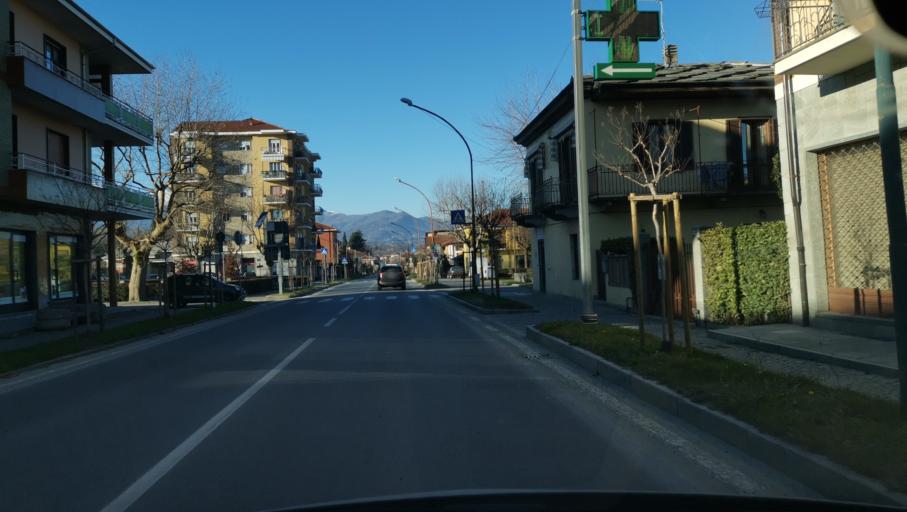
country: IT
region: Piedmont
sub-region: Provincia di Cuneo
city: Bagnolo Piemonte
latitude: 44.7619
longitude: 7.3147
